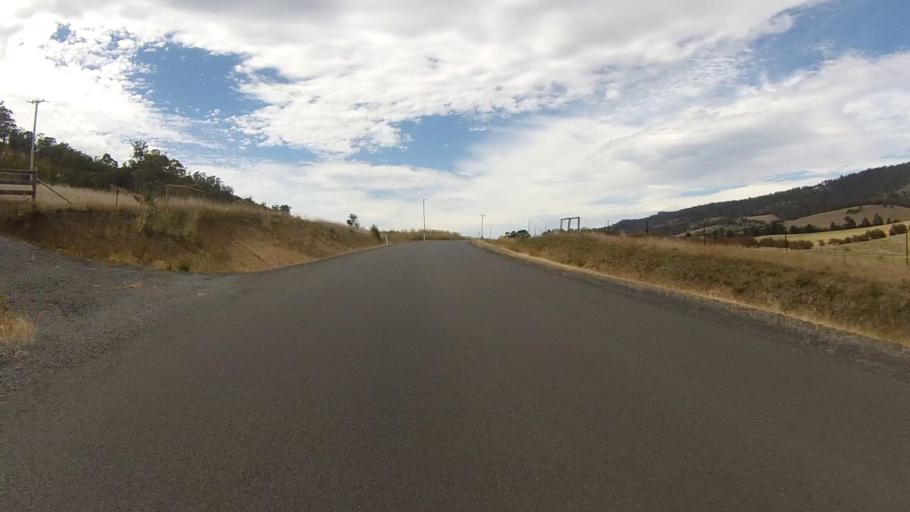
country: AU
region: Tasmania
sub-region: Brighton
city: Old Beach
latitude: -42.7227
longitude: 147.3399
